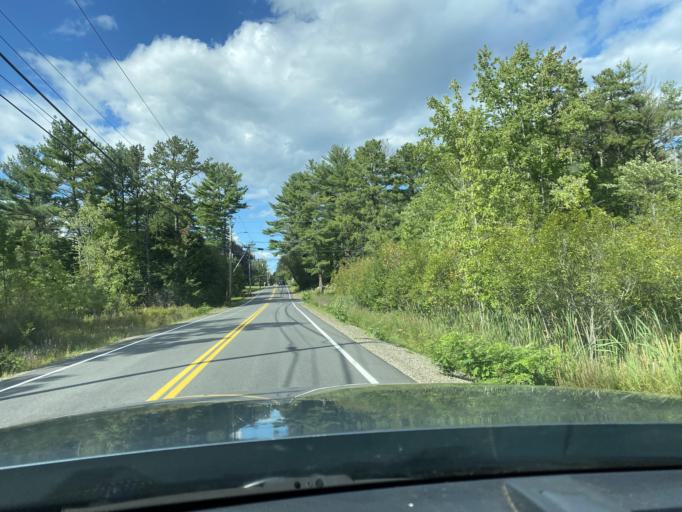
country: US
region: Maine
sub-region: York County
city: York Harbor
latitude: 43.1528
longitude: -70.7119
